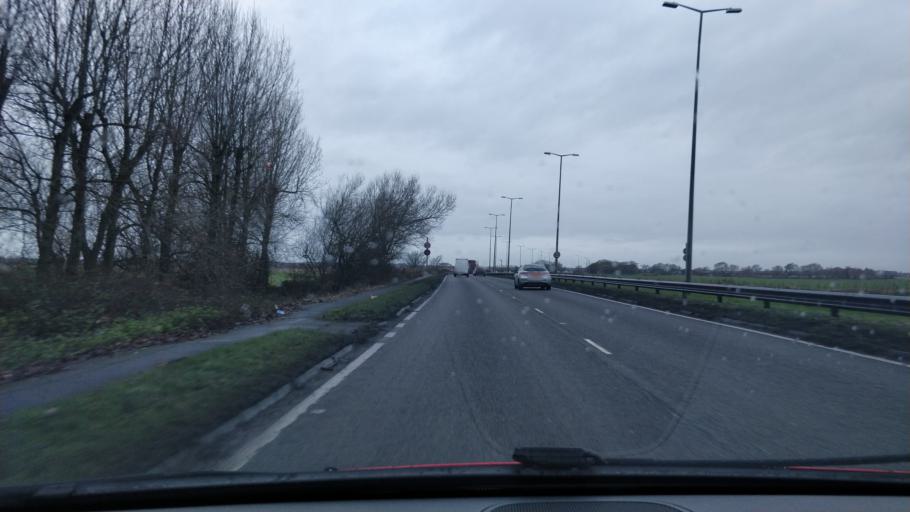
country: GB
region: England
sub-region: Sefton
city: Ince Blundell
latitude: 53.5304
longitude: -3.0360
